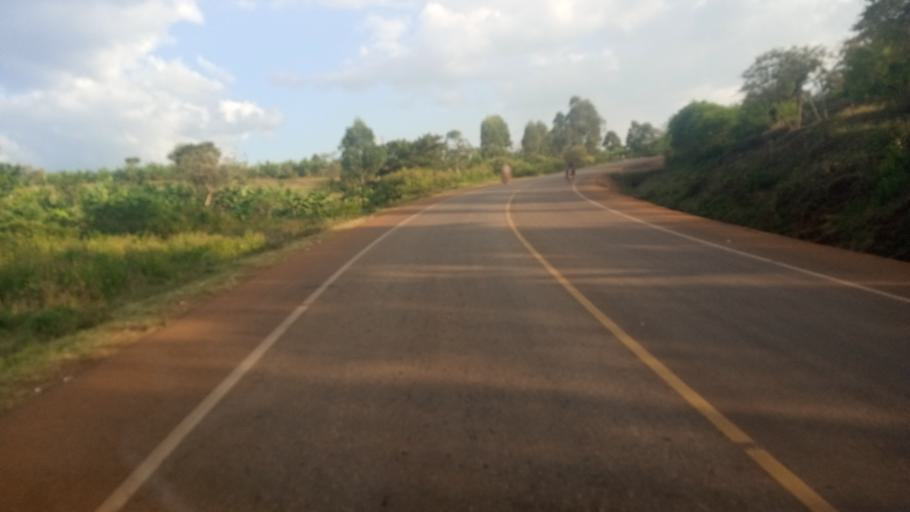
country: UG
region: Eastern Region
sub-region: Sironko District
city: Sironko
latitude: 1.3272
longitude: 34.3295
